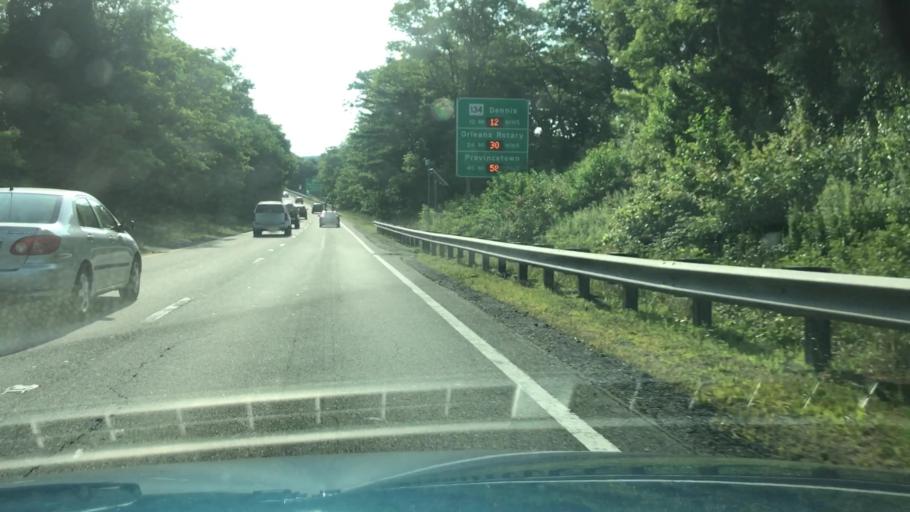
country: US
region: Massachusetts
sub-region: Barnstable County
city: West Barnstable
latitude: 41.6840
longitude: -70.3531
